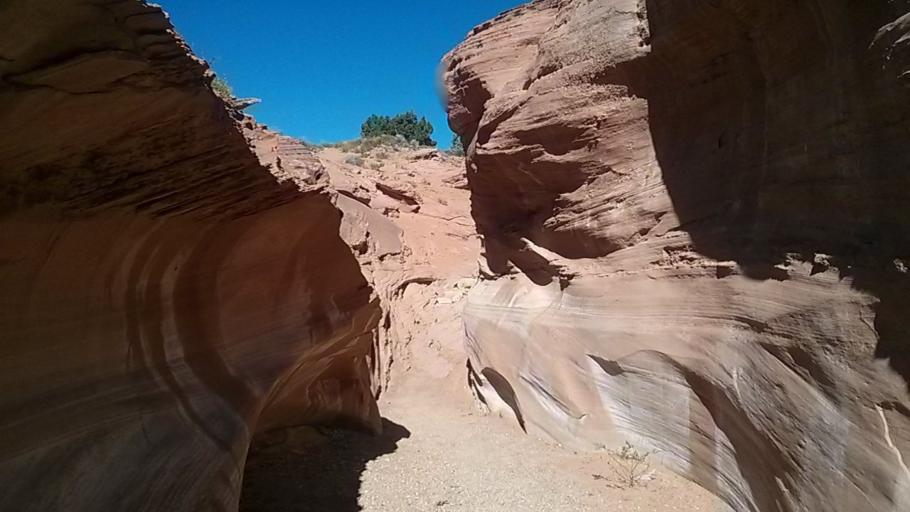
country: US
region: Arizona
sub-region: Coconino County
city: Page
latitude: 37.4825
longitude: -111.2279
